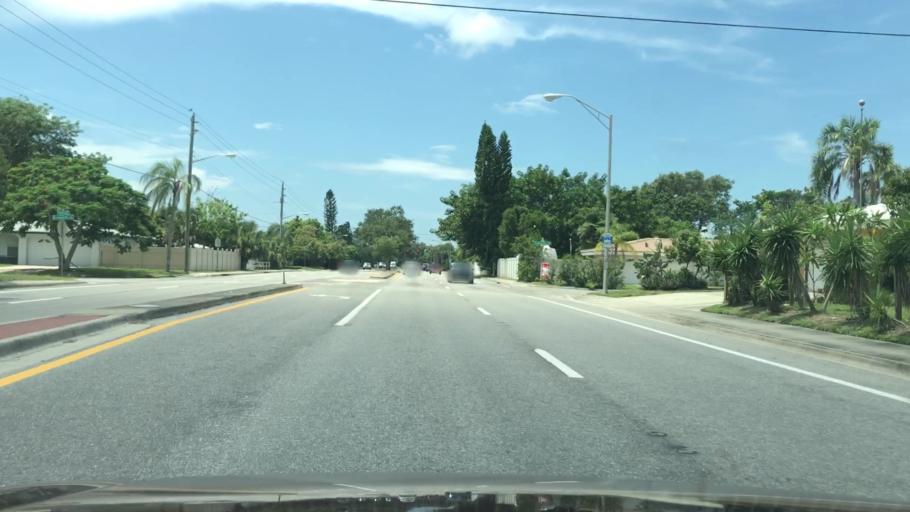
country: US
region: Florida
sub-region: Sarasota County
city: Southgate
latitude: 27.3110
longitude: -82.5142
